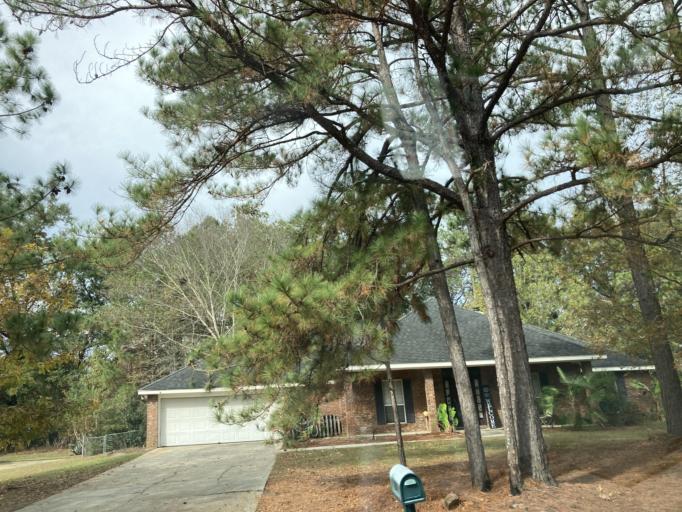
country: US
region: Mississippi
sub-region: Lamar County
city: West Hattiesburg
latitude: 31.2855
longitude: -89.3641
